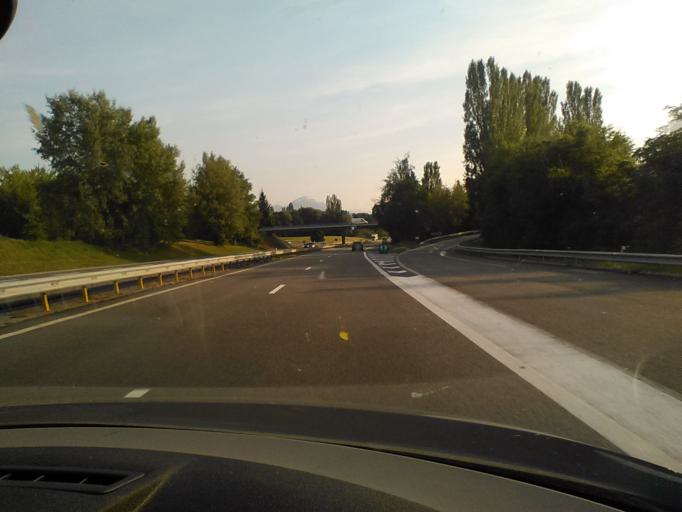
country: FR
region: Rhone-Alpes
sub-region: Departement de la Savoie
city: Drumettaz-Clarafond
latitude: 45.6544
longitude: 5.9260
